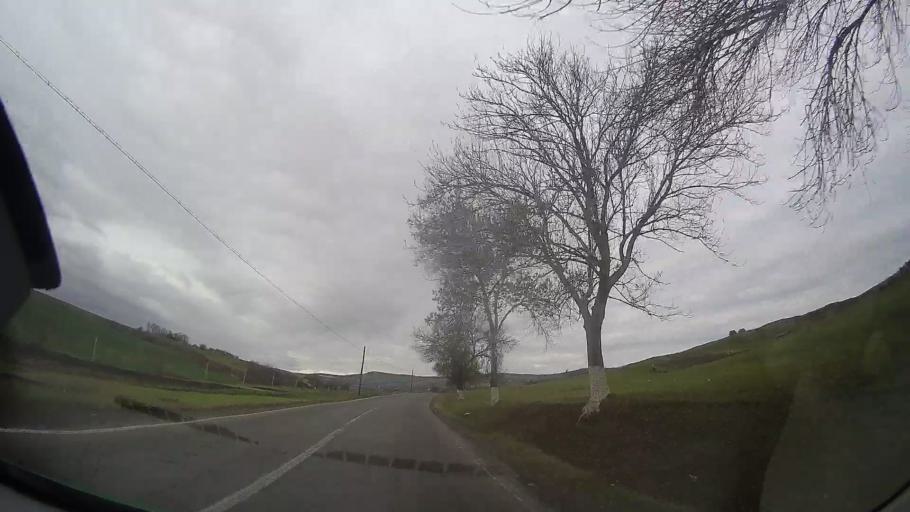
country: RO
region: Bistrita-Nasaud
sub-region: Comuna Urmenis
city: Urmenis
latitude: 46.7619
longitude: 24.3811
